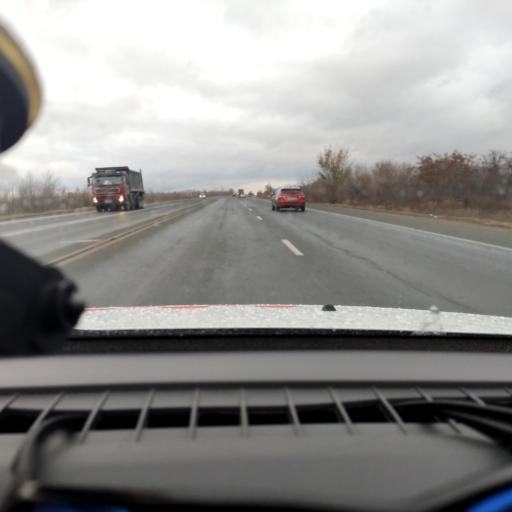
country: RU
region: Samara
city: Novokuybyshevsk
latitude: 53.0766
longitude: 50.0389
